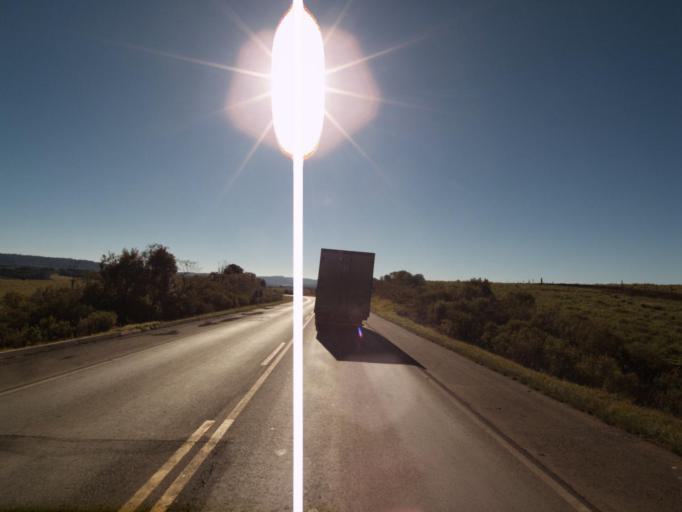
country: BR
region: Santa Catarina
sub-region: Concordia
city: Concordia
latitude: -26.9486
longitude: -51.8265
